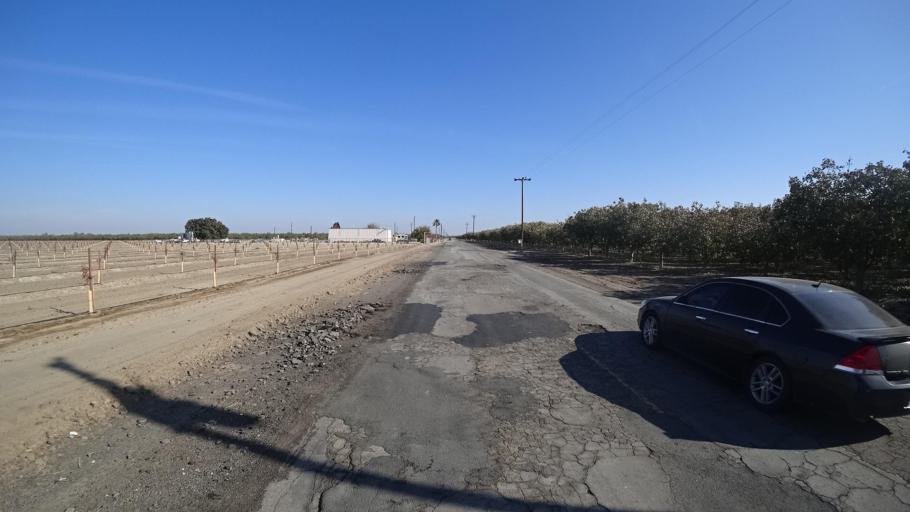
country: US
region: California
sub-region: Kern County
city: Wasco
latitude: 35.6524
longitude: -119.3423
